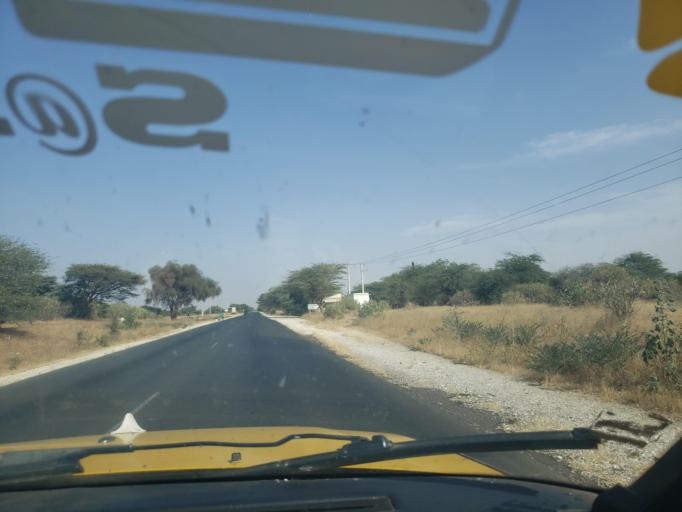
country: SN
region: Saint-Louis
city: Saint-Louis
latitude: 15.9264
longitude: -16.3672
